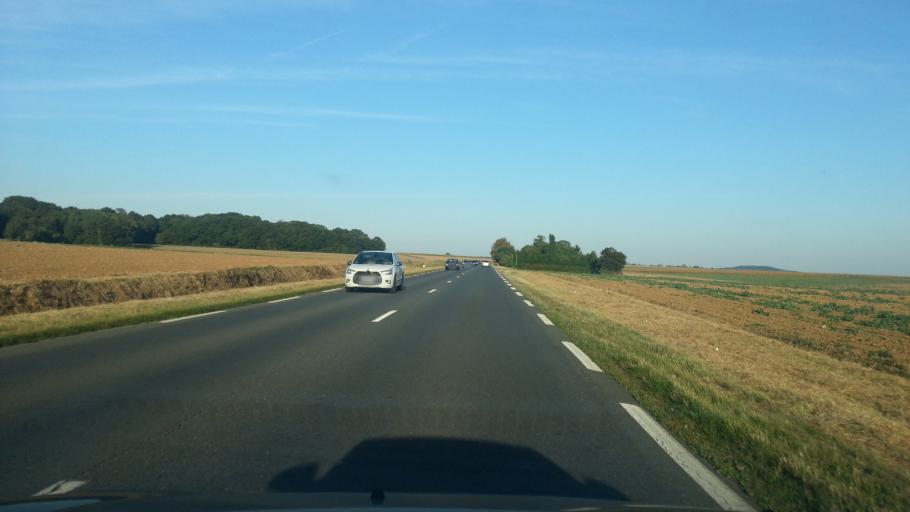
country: FR
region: Picardie
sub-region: Departement de l'Oise
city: Sacy-le-Grand
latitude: 49.3772
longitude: 2.5408
